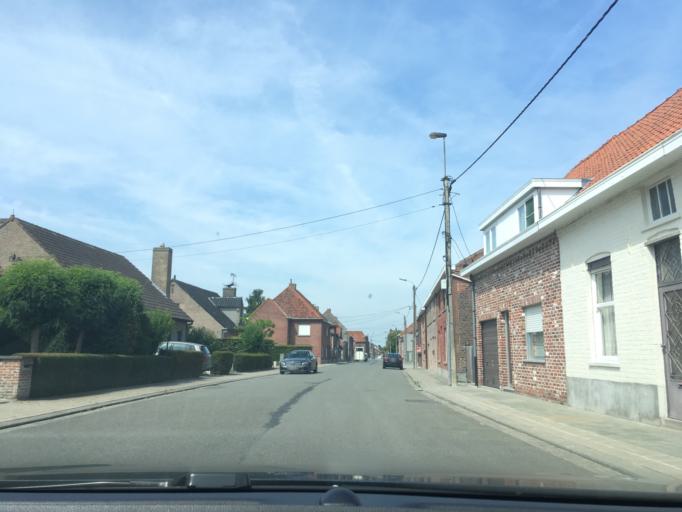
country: BE
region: Flanders
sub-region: Provincie West-Vlaanderen
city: Ledegem
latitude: 50.8918
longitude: 3.1172
